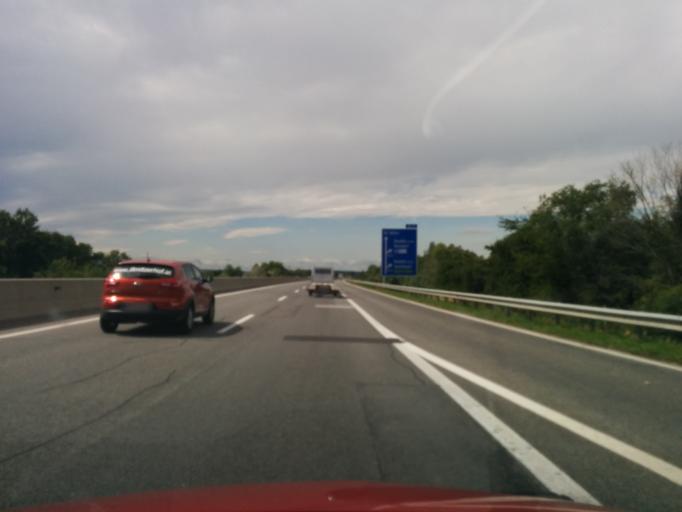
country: AT
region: Burgenland
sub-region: Politischer Bezirk Neusiedl am See
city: Parndorf
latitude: 47.9706
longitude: 16.8727
